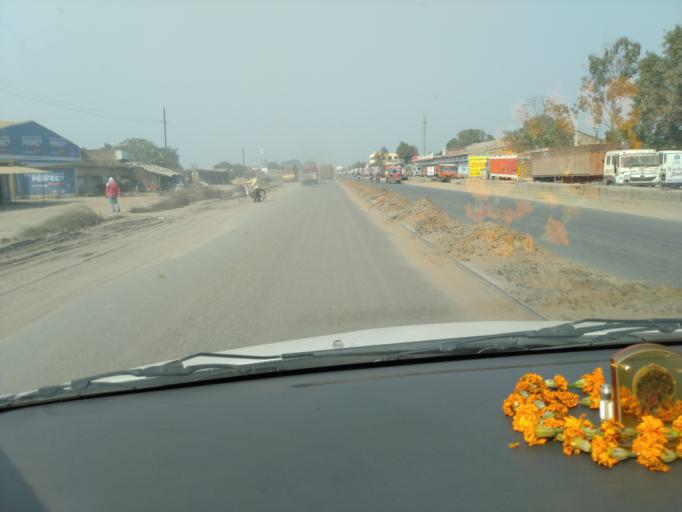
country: IN
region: Bihar
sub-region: Rohtas
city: Dehri
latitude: 24.9161
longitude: 84.1563
